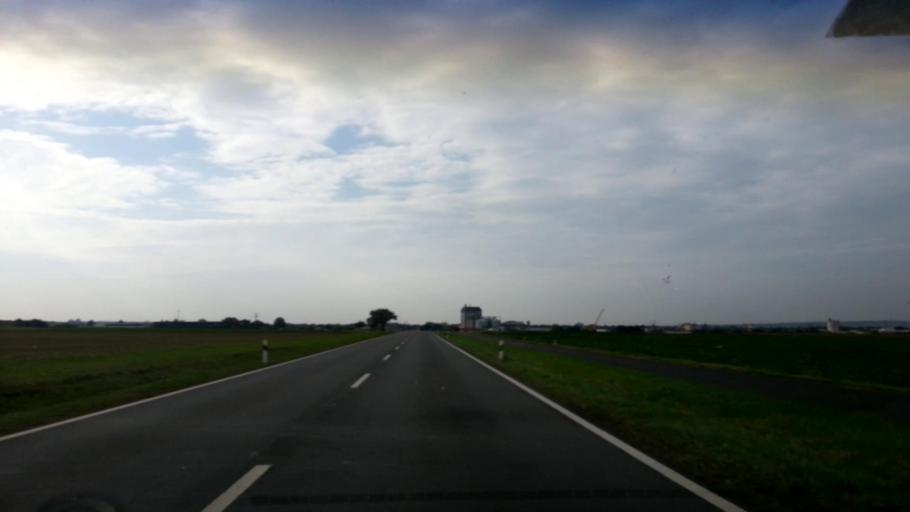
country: DE
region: Bavaria
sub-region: Regierungsbezirk Unterfranken
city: Gerolzhofen
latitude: 49.9143
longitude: 10.3547
